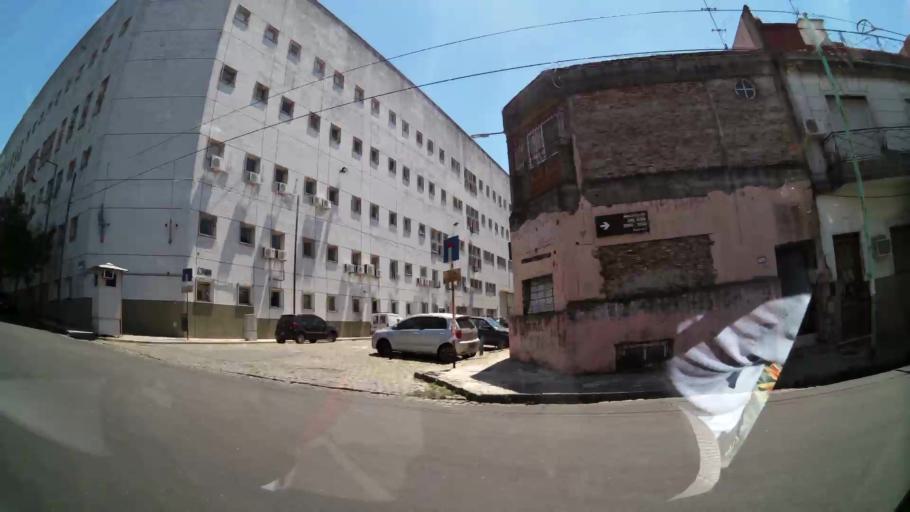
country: AR
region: Buenos Aires F.D.
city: Buenos Aires
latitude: -34.6367
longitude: -58.3791
